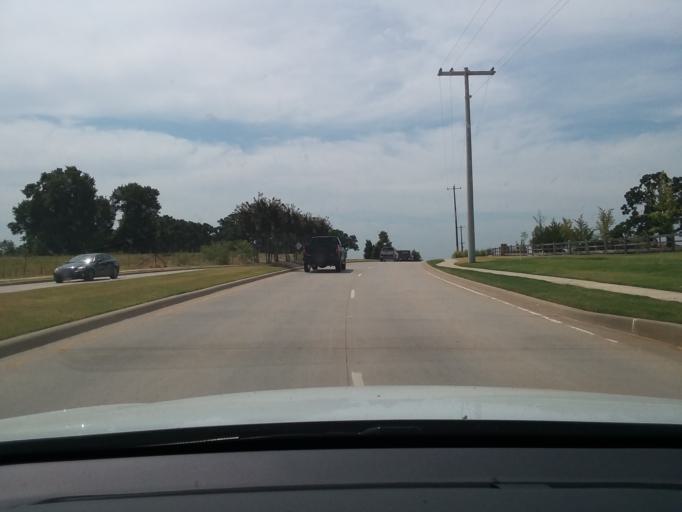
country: US
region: Texas
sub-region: Denton County
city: Flower Mound
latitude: 33.0391
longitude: -97.1057
